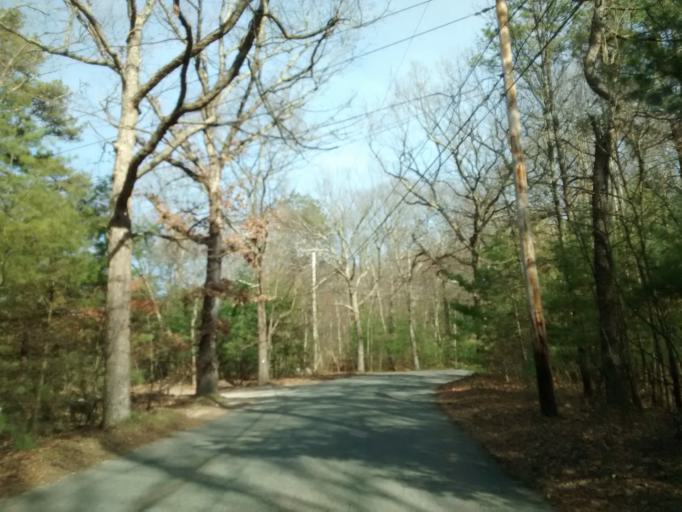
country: US
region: Massachusetts
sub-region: Worcester County
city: Millville
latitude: 42.0260
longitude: -71.6009
